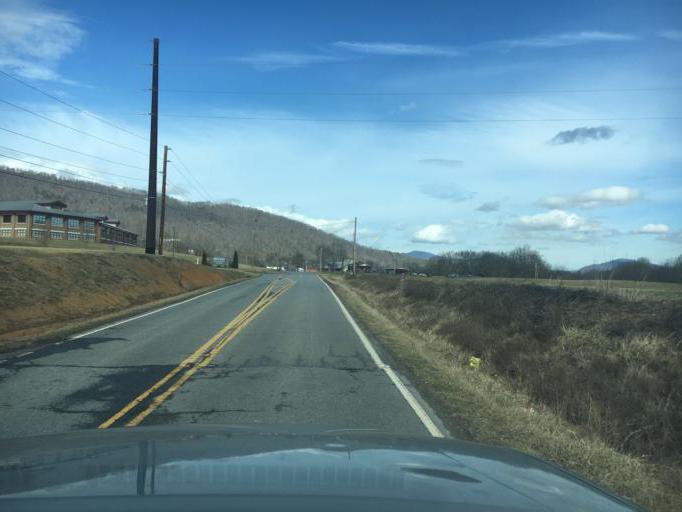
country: US
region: North Carolina
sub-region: Haywood County
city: Clyde
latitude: 35.4833
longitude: -82.8874
